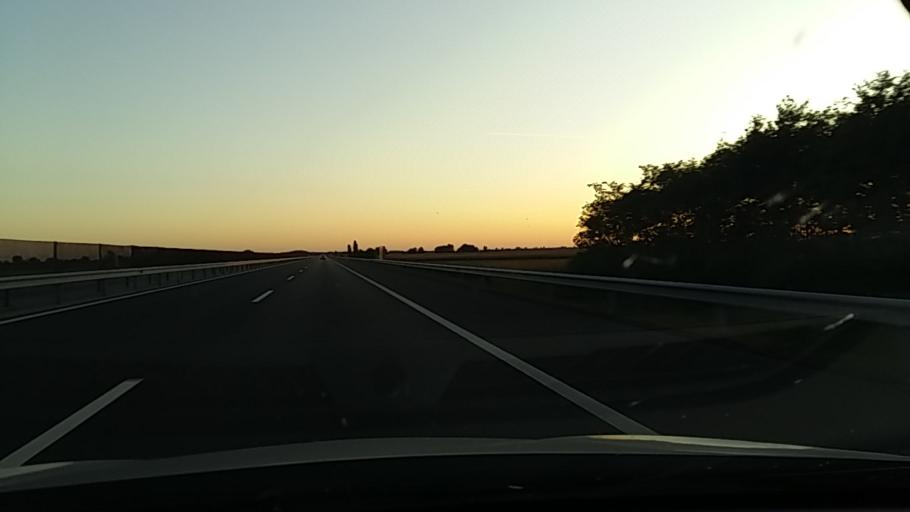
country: HU
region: Hajdu-Bihar
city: Gorbehaza
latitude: 47.8143
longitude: 21.3108
